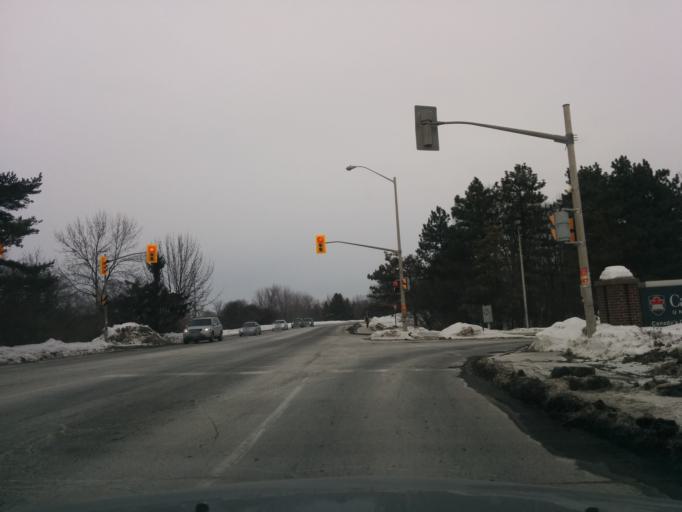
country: CA
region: Ontario
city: Ottawa
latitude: 45.3785
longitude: -75.7013
